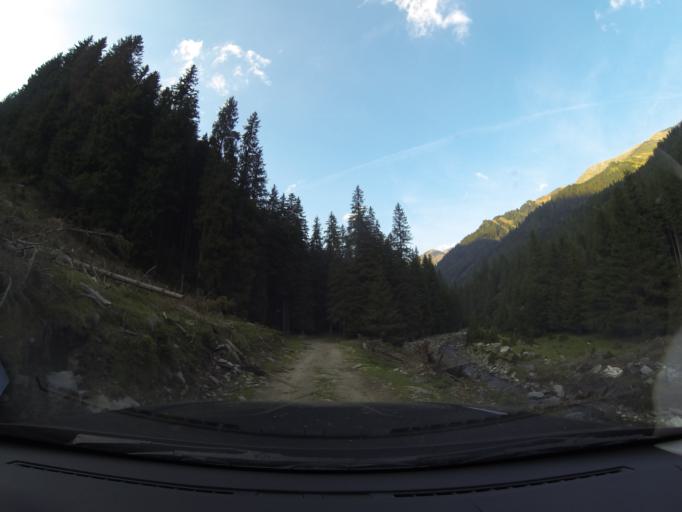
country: RO
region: Brasov
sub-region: Oras Victoria
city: Victoria
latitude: 45.5713
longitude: 24.6999
